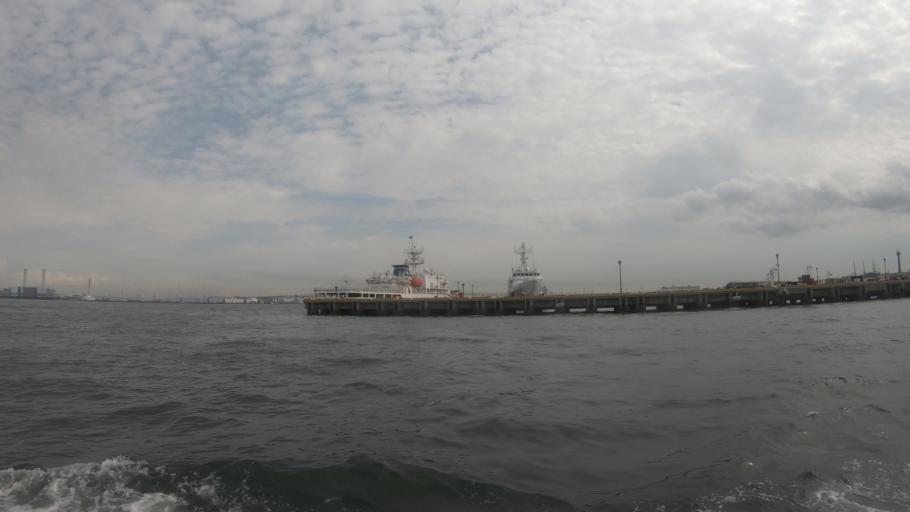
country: JP
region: Kanagawa
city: Yokohama
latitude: 35.4579
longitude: 139.6444
